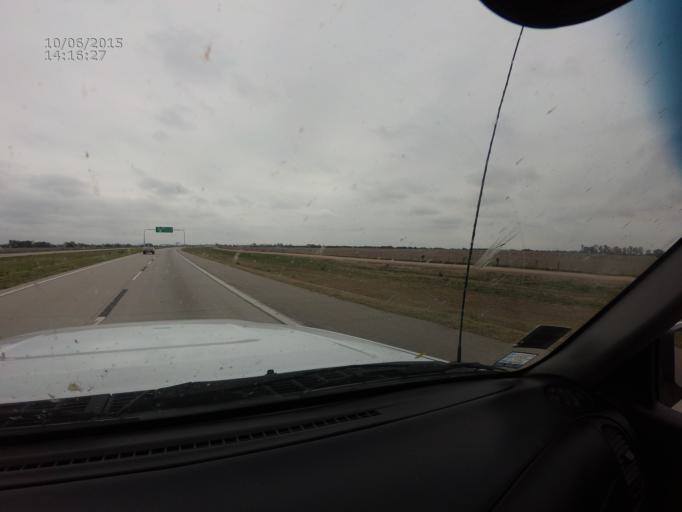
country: AR
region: Cordoba
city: Villa Maria
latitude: -32.3995
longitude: -63.1935
